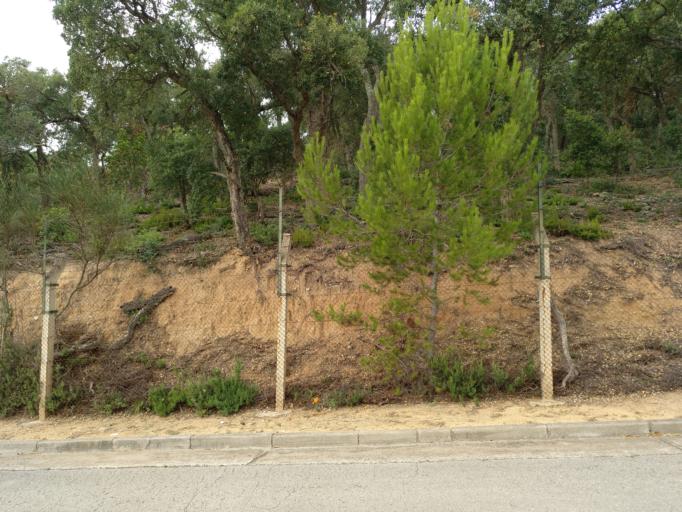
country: ES
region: Catalonia
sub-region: Provincia de Girona
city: Tossa de Mar
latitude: 41.7180
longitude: 2.8988
